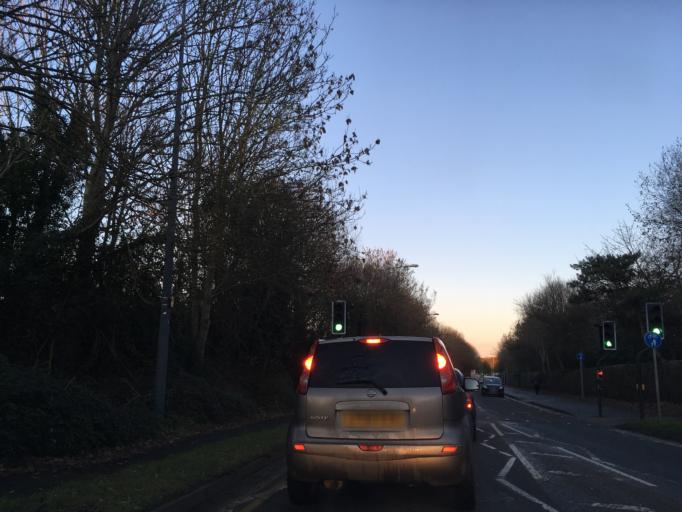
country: GB
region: England
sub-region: South Gloucestershire
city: Stoke Gifford
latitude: 51.5116
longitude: -2.5506
